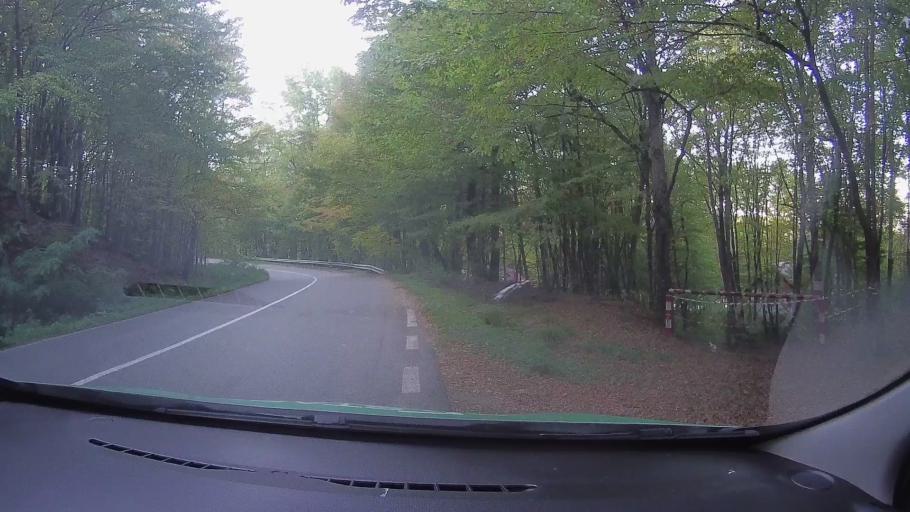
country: RO
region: Timis
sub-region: Comuna Fardea
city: Fardea
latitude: 45.7515
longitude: 22.1267
